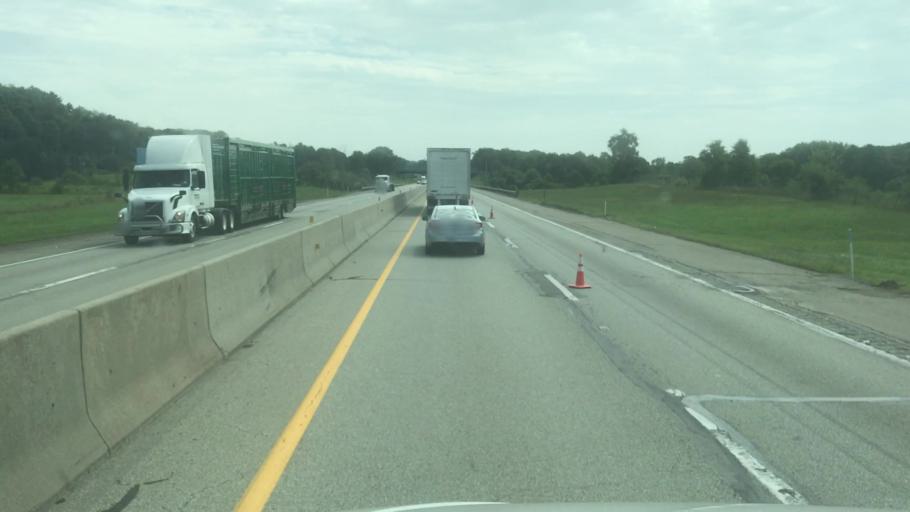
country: US
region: Pennsylvania
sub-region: Butler County
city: Fernway
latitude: 40.7393
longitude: -80.1859
